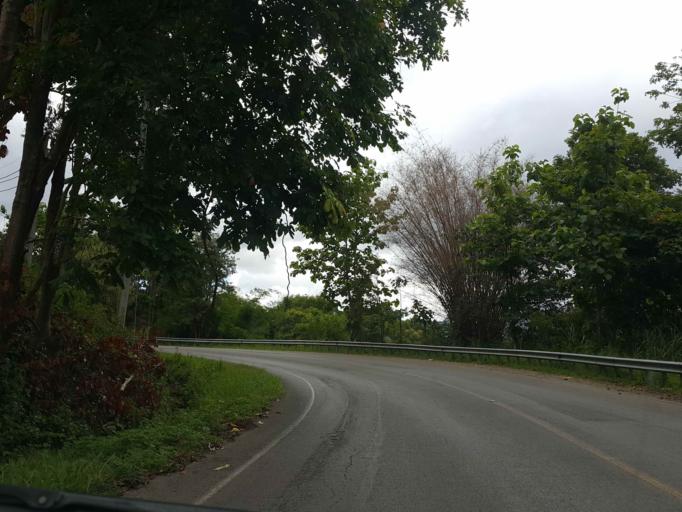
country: TH
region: Chiang Mai
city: Samoeng
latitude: 18.8001
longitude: 98.8321
